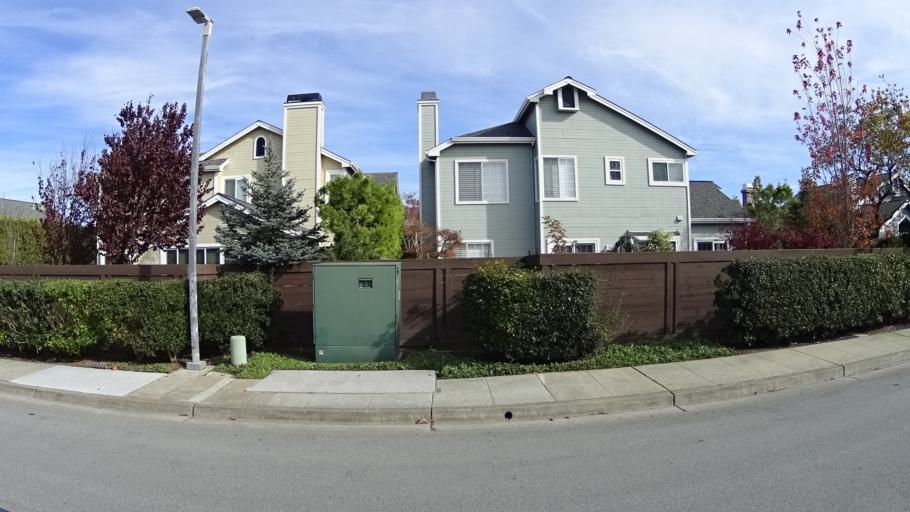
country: US
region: California
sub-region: San Mateo County
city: Redwood Shores
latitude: 37.5419
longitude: -122.2606
